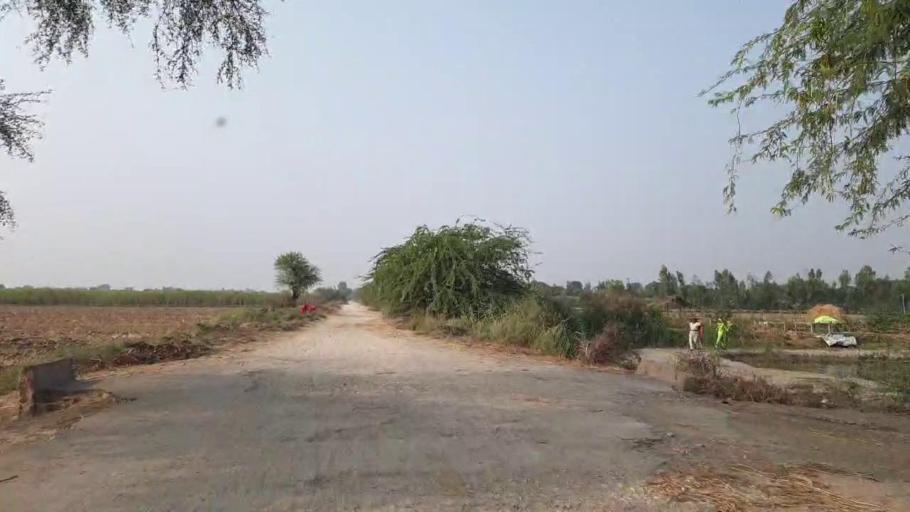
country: PK
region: Sindh
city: Tando Muhammad Khan
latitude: 25.0783
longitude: 68.5899
